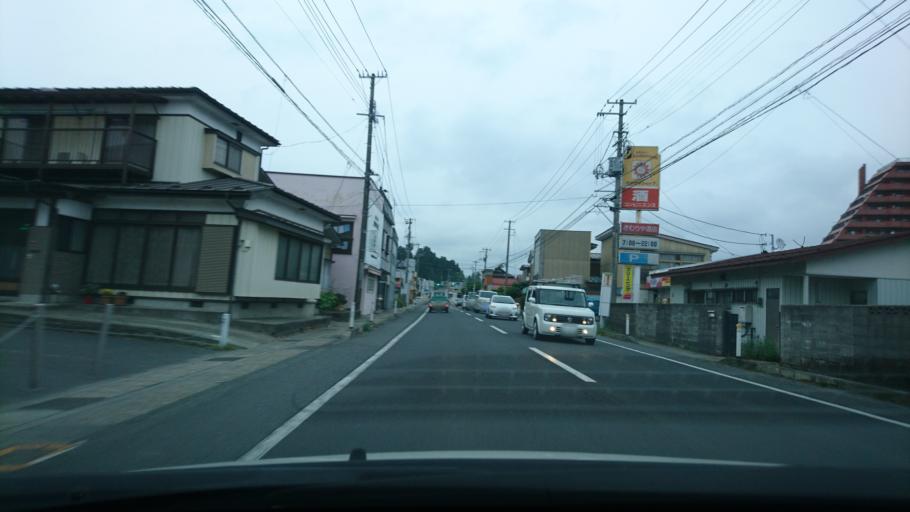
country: JP
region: Iwate
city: Ichinoseki
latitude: 38.9179
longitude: 141.1319
